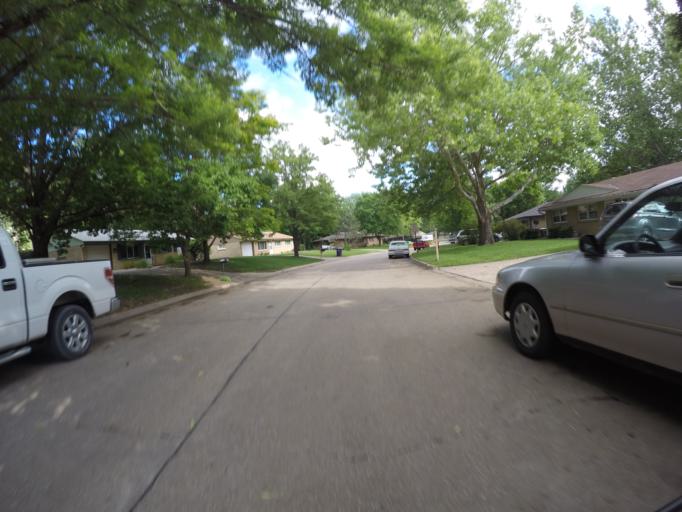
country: US
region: Kansas
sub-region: Riley County
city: Manhattan
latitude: 39.2005
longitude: -96.6023
